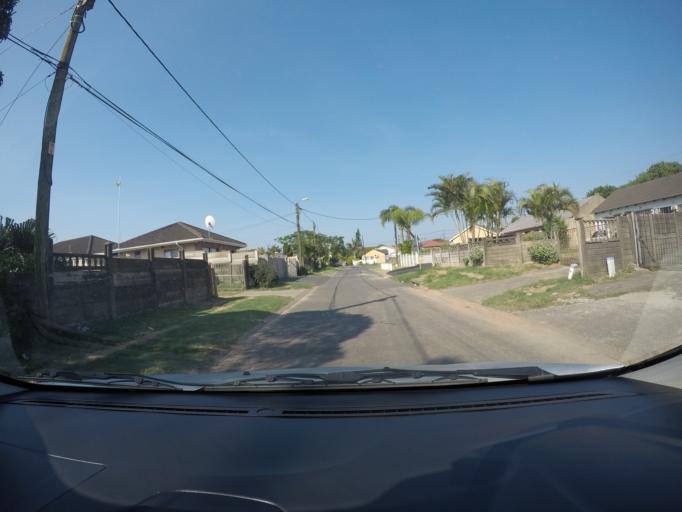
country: ZA
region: KwaZulu-Natal
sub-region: uThungulu District Municipality
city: Richards Bay
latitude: -28.7171
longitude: 32.0401
